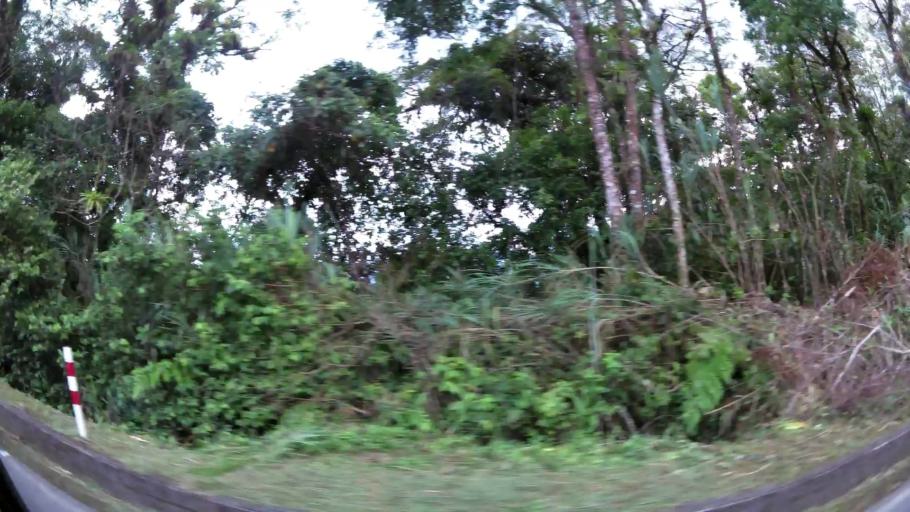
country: EC
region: Pastaza
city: Puyo
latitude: -1.4583
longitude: -78.1181
